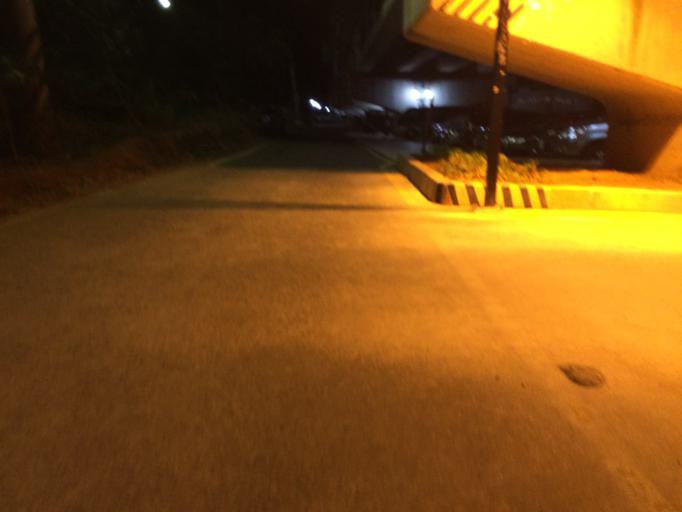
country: TW
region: Taiwan
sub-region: Hsinchu
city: Zhubei
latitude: 24.7863
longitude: 121.0226
